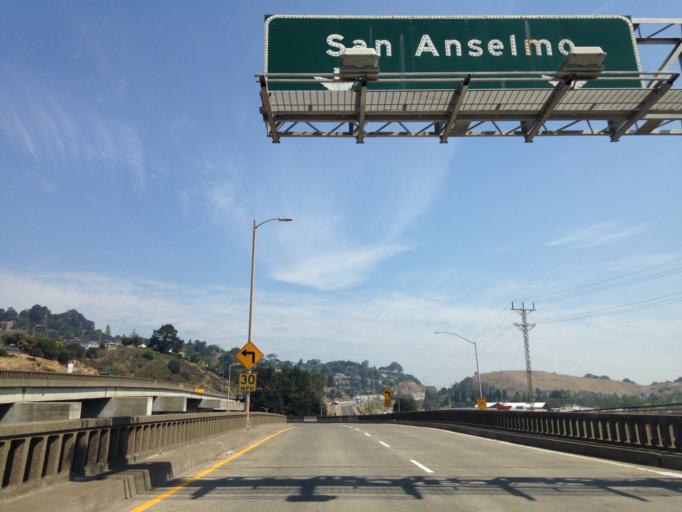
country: US
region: California
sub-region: Marin County
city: Corte Madera
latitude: 37.9432
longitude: -122.5149
